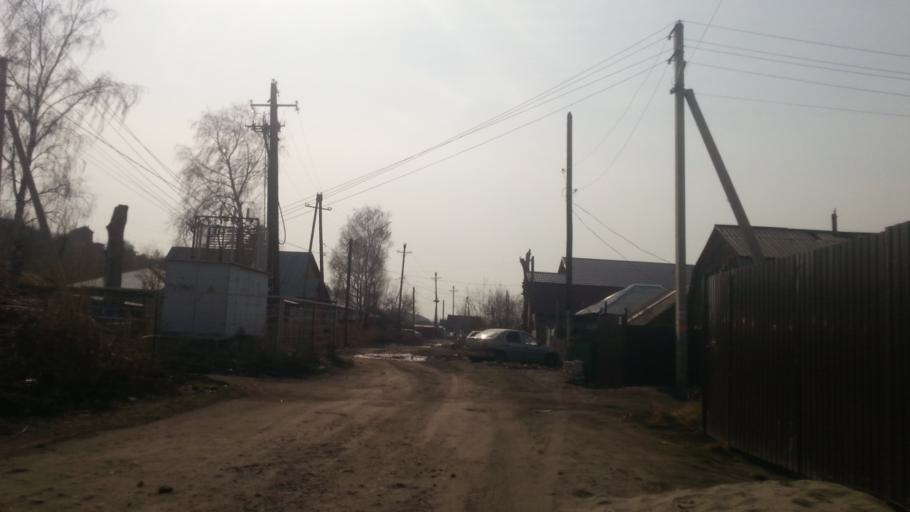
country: RU
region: Altai Krai
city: Zaton
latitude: 53.3215
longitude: 83.7782
